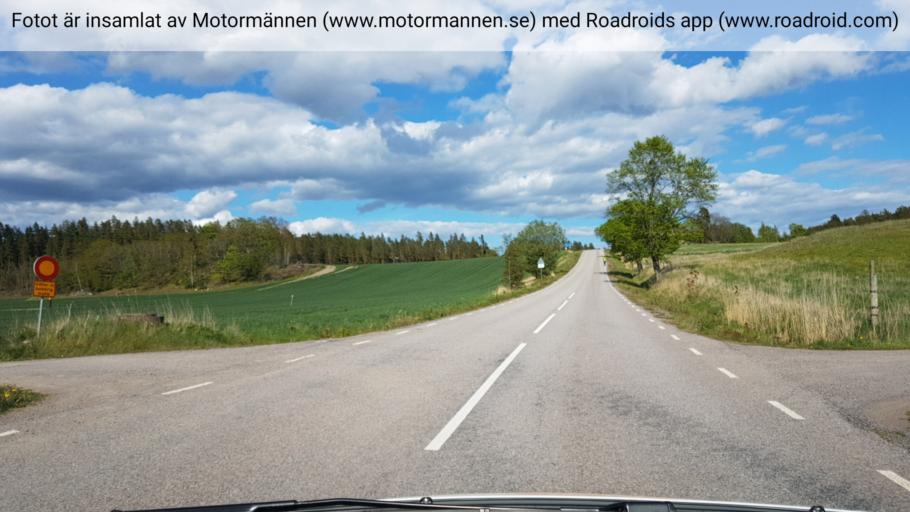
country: SE
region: Kalmar
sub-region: Vasterviks Kommun
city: Gamleby
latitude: 57.9207
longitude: 16.4190
